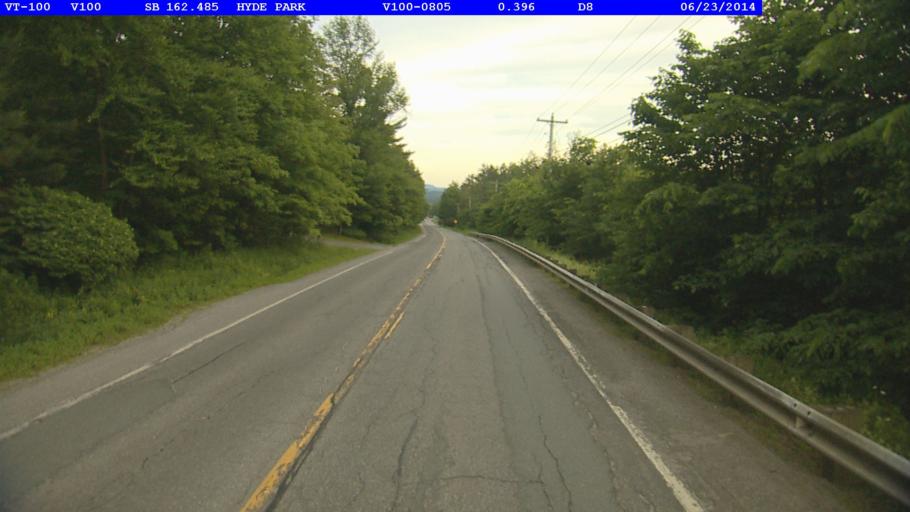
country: US
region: Vermont
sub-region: Lamoille County
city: Hyde Park
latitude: 44.6026
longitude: -72.6148
